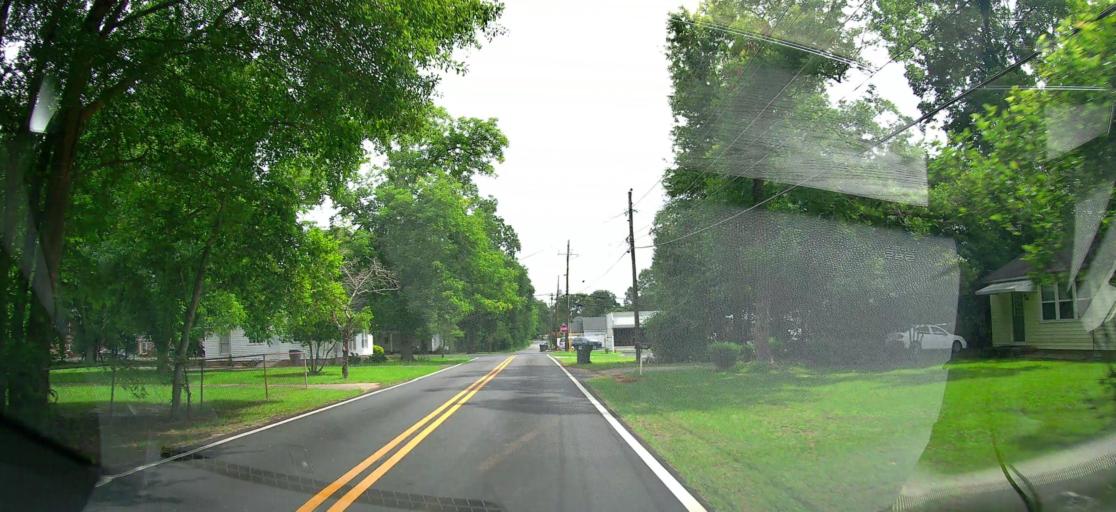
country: US
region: Georgia
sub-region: Peach County
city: Byron
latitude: 32.6525
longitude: -83.7583
